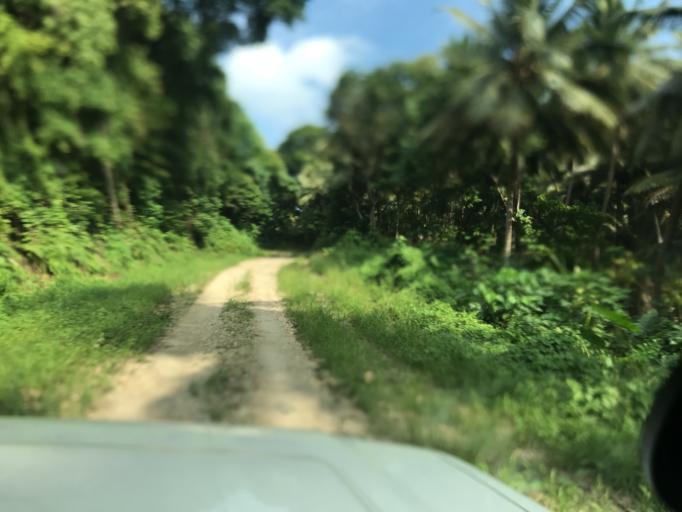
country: VU
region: Sanma
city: Luganville
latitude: -15.6181
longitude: 166.7834
